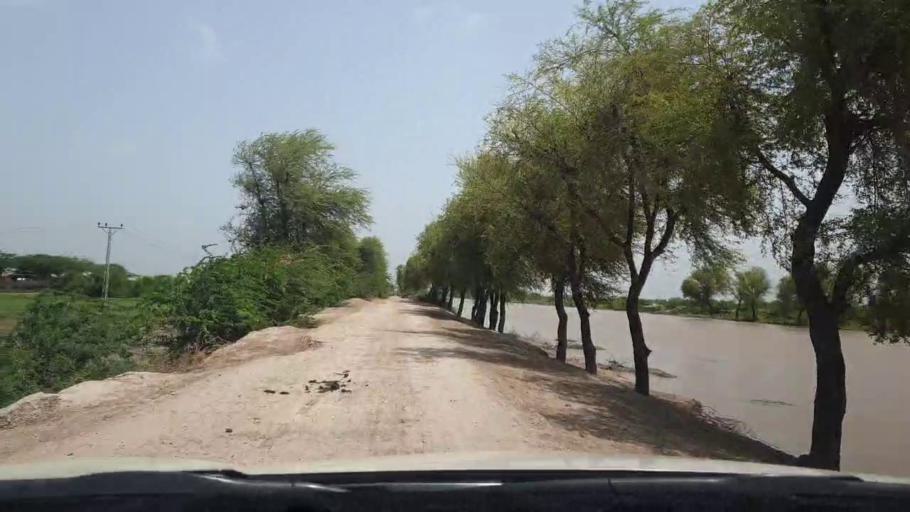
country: PK
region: Sindh
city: Talhar
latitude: 24.9185
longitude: 68.8392
